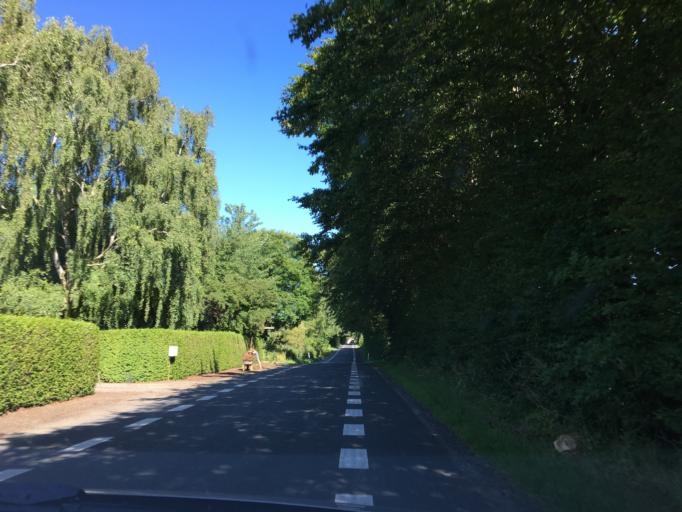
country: DK
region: South Denmark
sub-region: Svendborg Kommune
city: Thuro By
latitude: 55.0457
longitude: 10.6962
